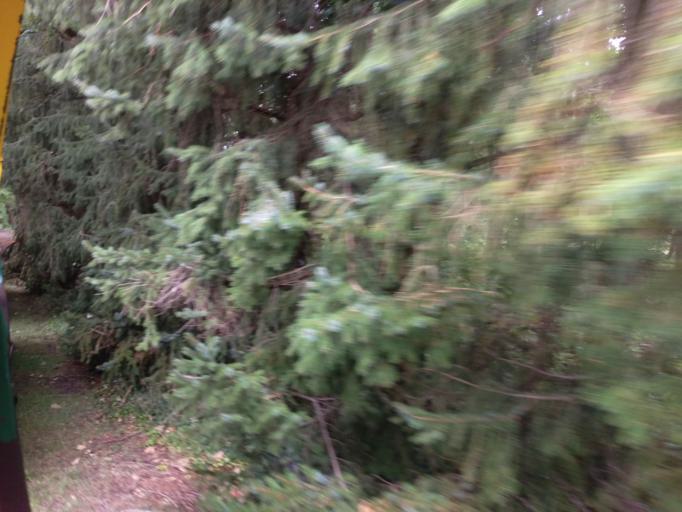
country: DE
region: Lower Saxony
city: Uetze
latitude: 52.4727
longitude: 10.2321
